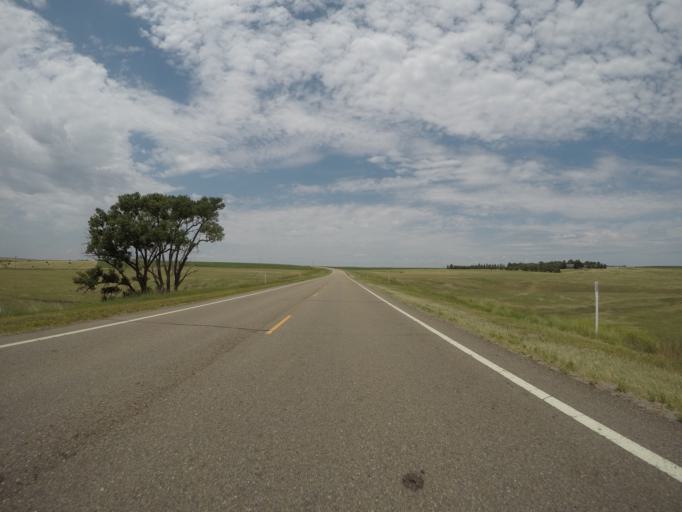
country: US
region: Kansas
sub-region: Thomas County
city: Colby
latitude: 39.3901
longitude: -100.8295
